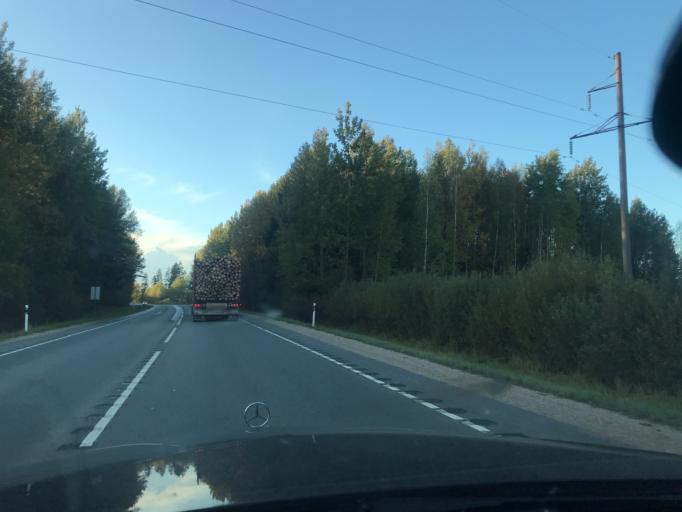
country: EE
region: Vorumaa
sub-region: Voru linn
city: Voru
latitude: 57.8627
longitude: 26.9659
